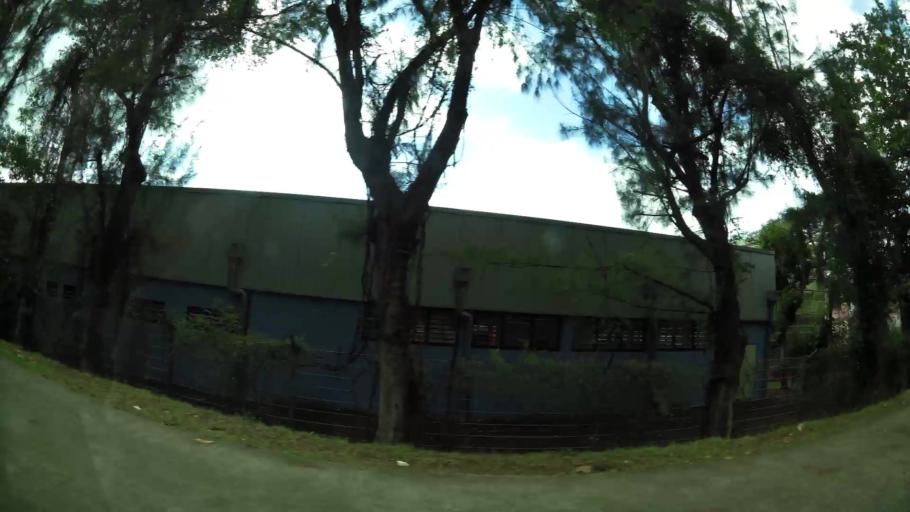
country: GP
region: Guadeloupe
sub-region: Guadeloupe
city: Pointe-a-Pitre
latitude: 16.2477
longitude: -61.5361
